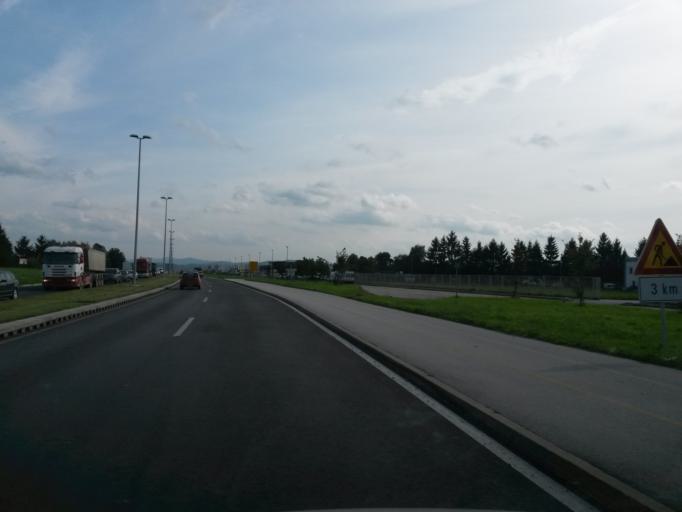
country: HR
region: Varazdinska
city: Varazdin
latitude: 46.2904
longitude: 16.3517
